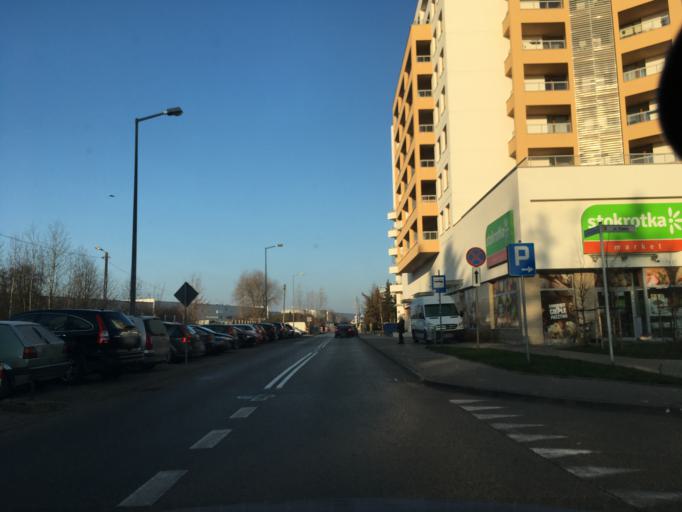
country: PL
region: Masovian Voivodeship
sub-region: Powiat piaseczynski
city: Piaseczno
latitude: 52.0767
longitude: 21.0113
